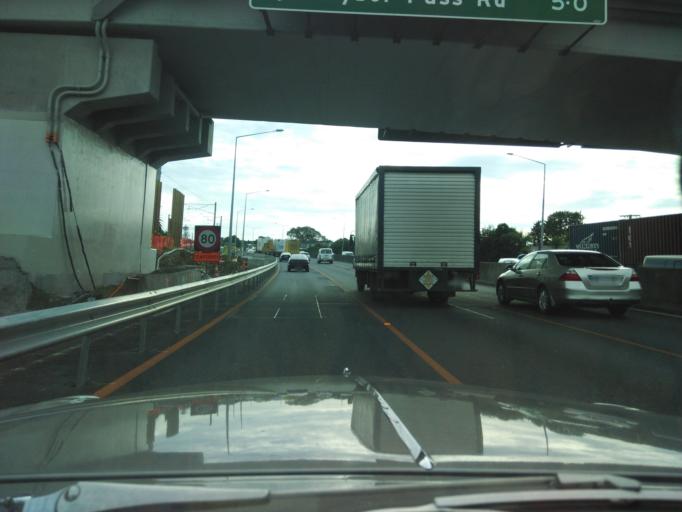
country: NZ
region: Auckland
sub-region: Auckland
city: Auckland
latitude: -36.8967
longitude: 174.8075
